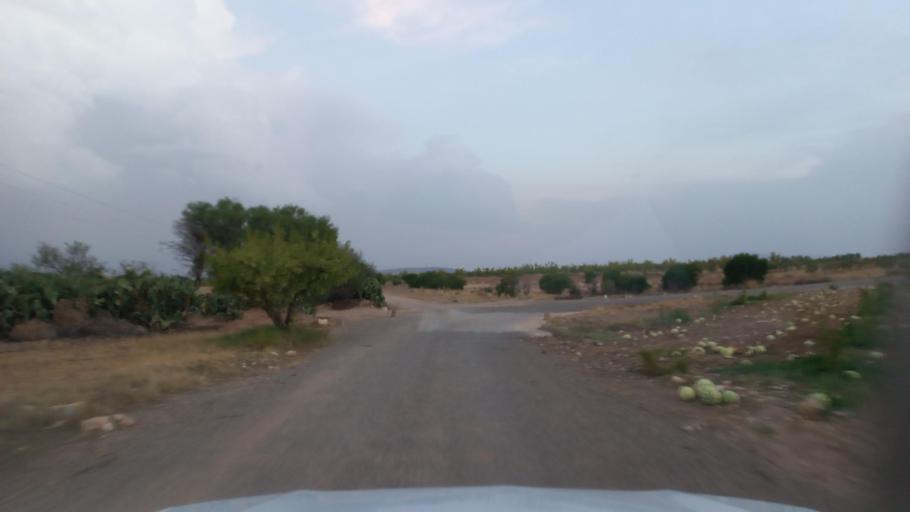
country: TN
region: Al Qasrayn
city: Kasserine
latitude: 35.2707
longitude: 9.0373
